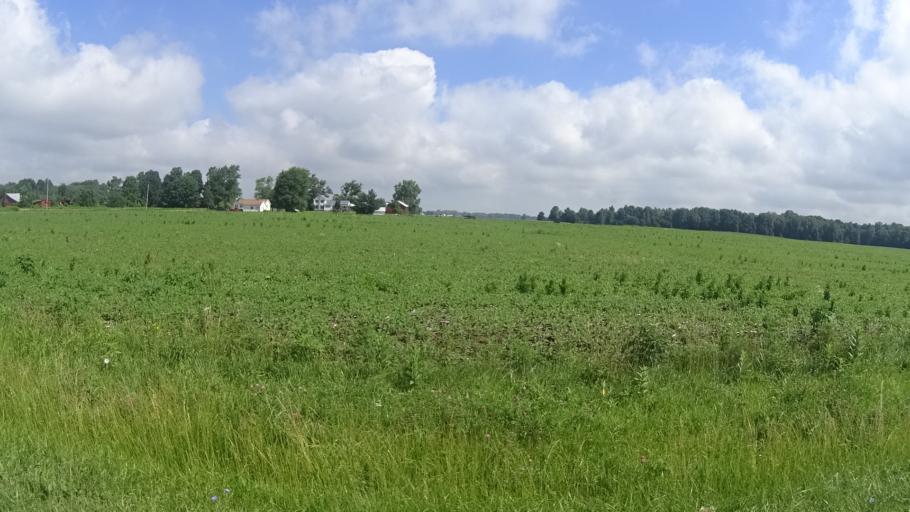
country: US
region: Ohio
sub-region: Huron County
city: Wakeman
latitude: 41.2839
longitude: -82.4412
